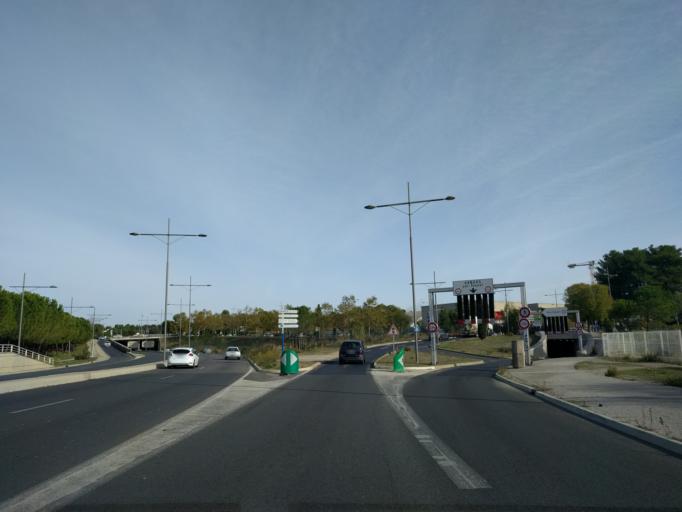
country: FR
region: Languedoc-Roussillon
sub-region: Departement de l'Herault
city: Montferrier-sur-Lez
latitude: 43.6379
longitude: 3.8461
